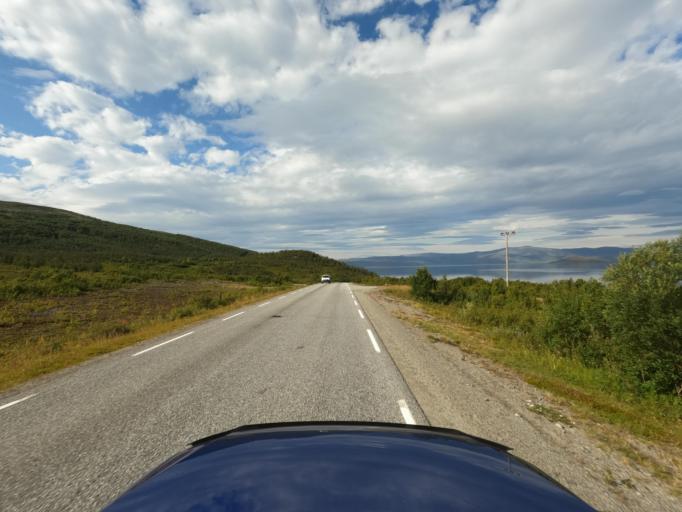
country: NO
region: Finnmark Fylke
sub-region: Kvalsund
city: Kvalsund
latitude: 70.4836
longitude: 24.1859
